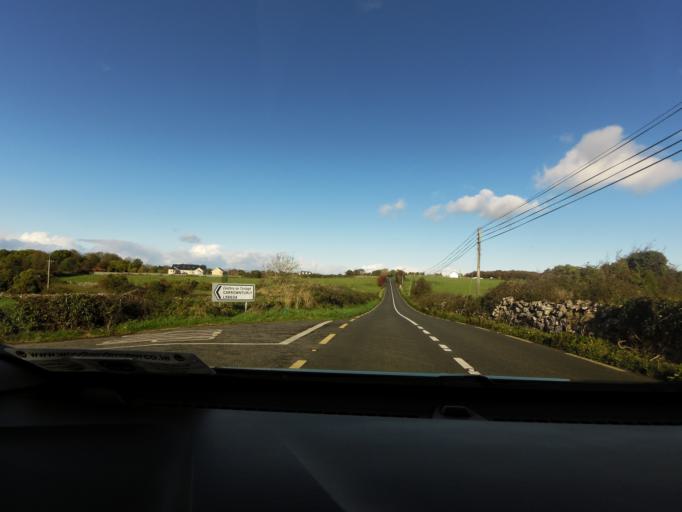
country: IE
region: Connaught
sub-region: Maigh Eo
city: Ballinrobe
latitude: 53.5665
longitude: -9.1174
